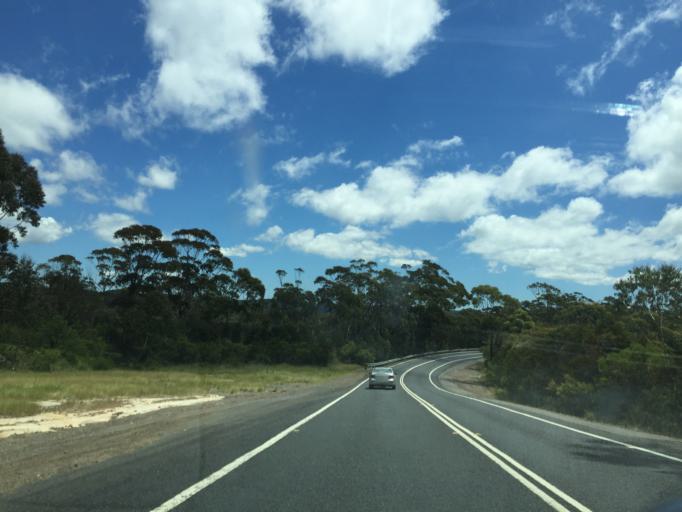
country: AU
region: New South Wales
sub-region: Blue Mountains Municipality
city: Blackheath
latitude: -33.5466
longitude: 150.3922
